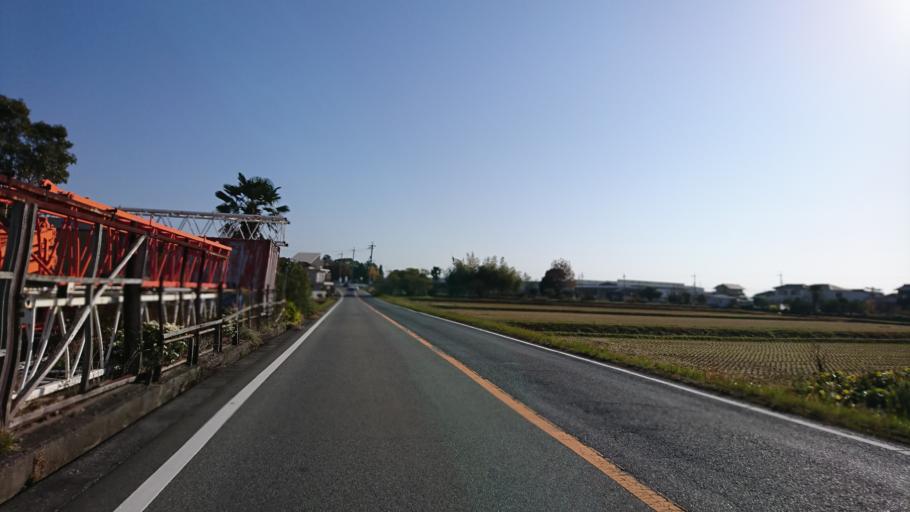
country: JP
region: Hyogo
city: Miki
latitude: 34.7608
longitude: 134.9274
